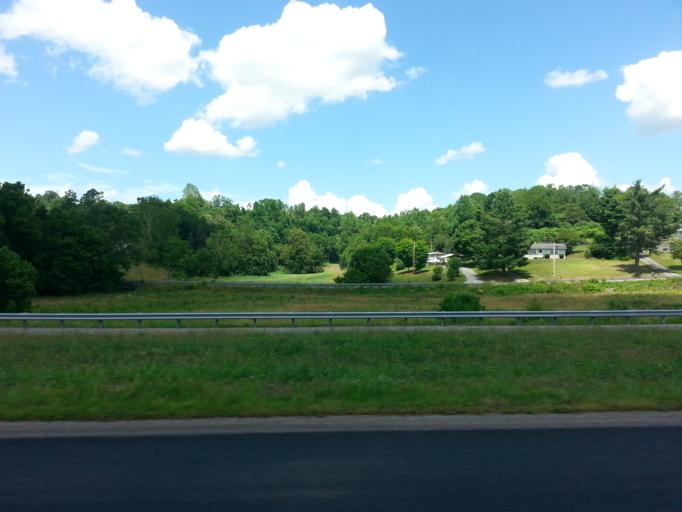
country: US
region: Virginia
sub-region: Lee County
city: Jonesville
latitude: 36.6713
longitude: -83.2037
